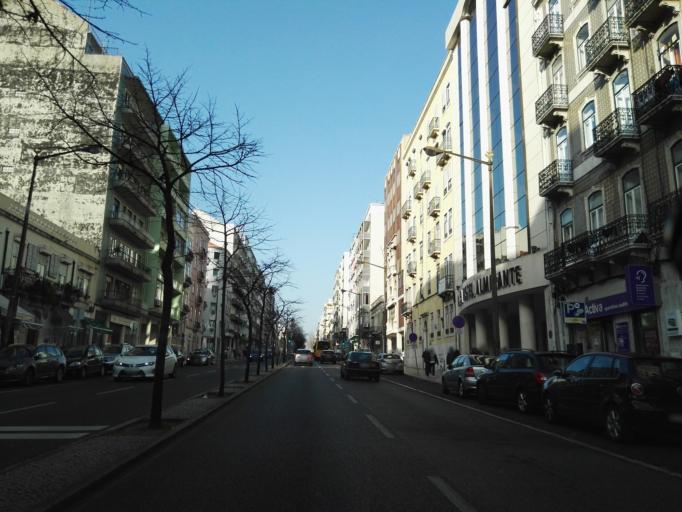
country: PT
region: Lisbon
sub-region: Lisbon
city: Lisbon
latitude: 38.7271
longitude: -9.1348
